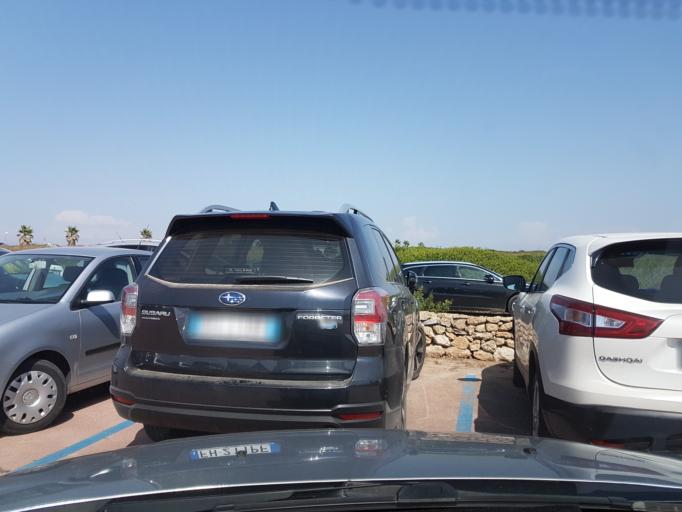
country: IT
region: Sardinia
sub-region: Provincia di Oristano
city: Cabras
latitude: 39.9526
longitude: 8.4033
